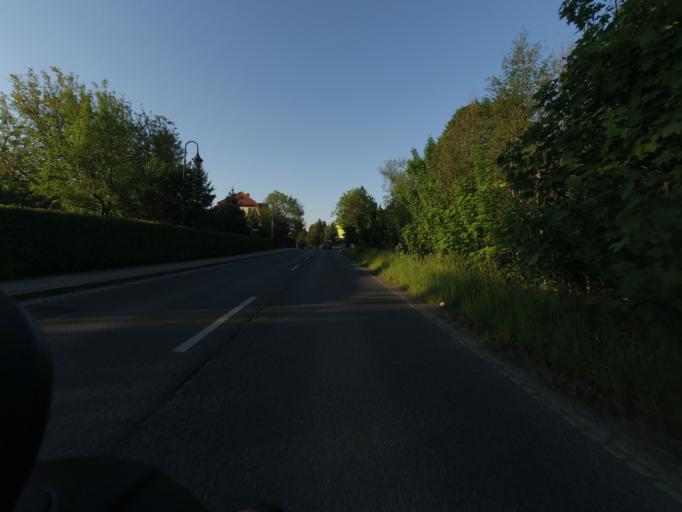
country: DE
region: Saxony
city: Kreischa
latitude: 50.9500
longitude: 13.7682
